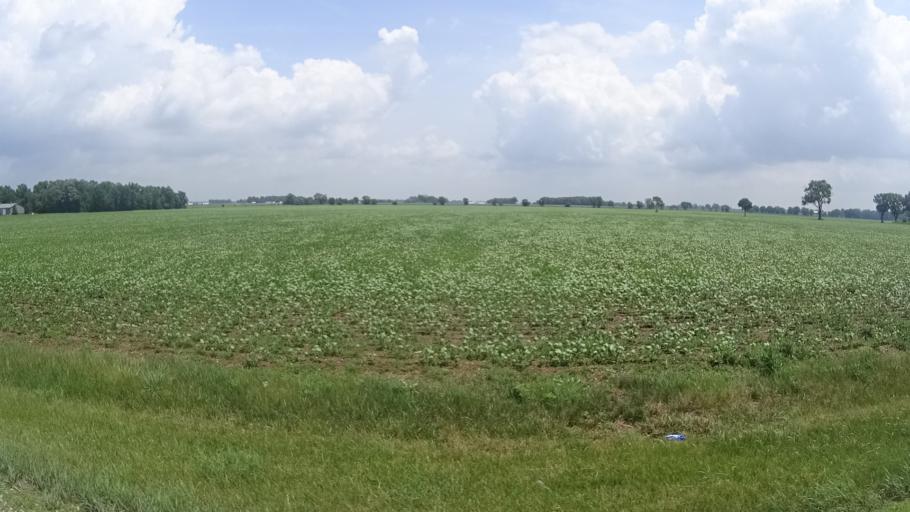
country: US
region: Ohio
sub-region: Huron County
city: Monroeville
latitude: 41.3317
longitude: -82.7473
